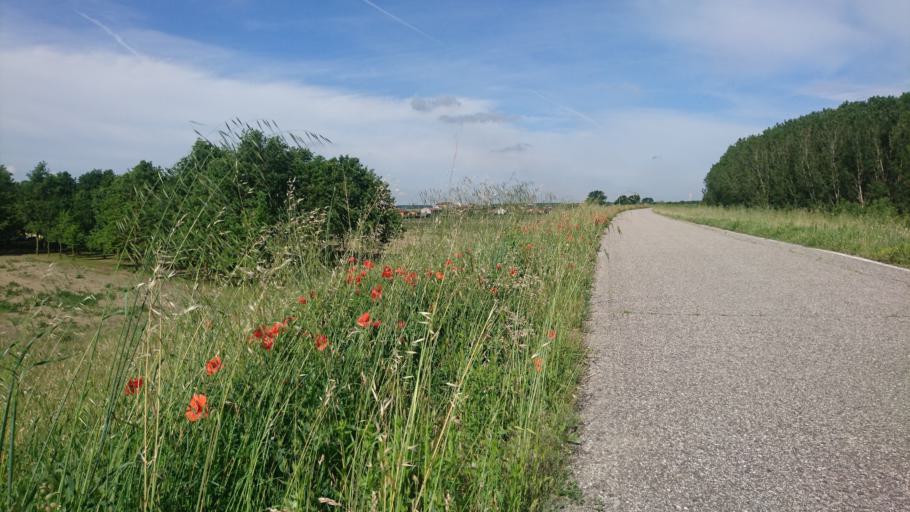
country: IT
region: Lombardy
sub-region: Provincia di Mantova
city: Carbonara di Po
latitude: 45.0392
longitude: 11.2271
